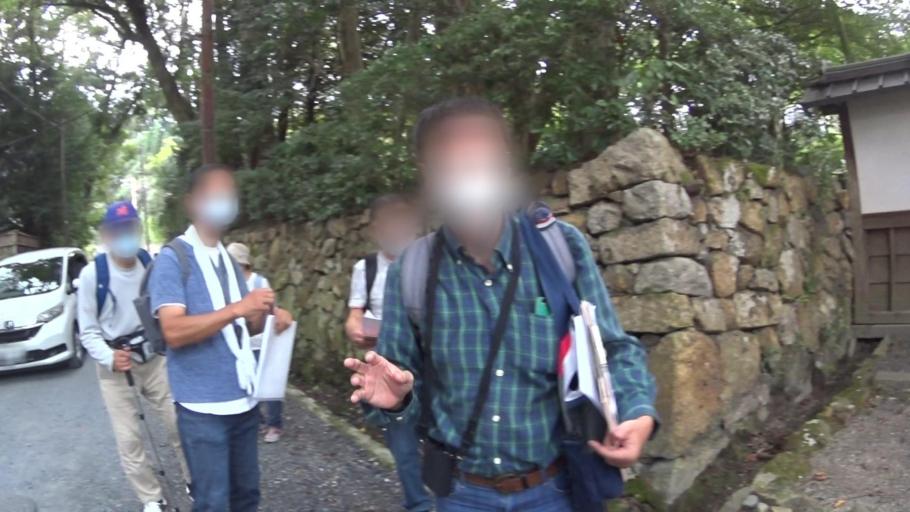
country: JP
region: Shiga Prefecture
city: Nagahama
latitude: 35.3982
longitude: 136.2372
